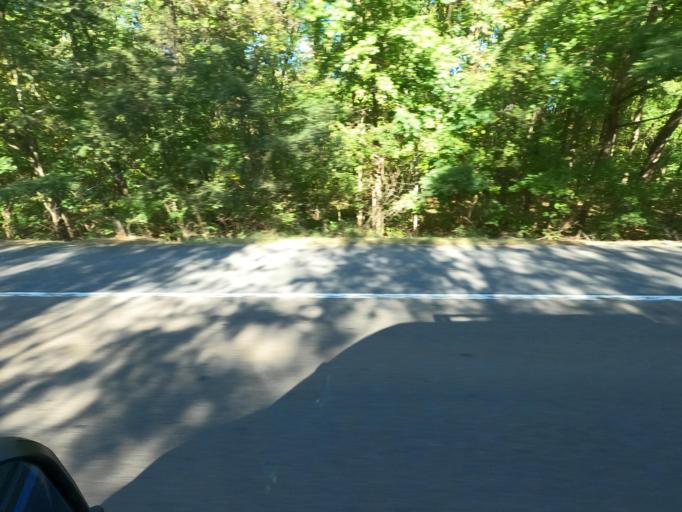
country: US
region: Tennessee
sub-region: Tipton County
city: Munford
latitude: 35.4350
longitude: -89.8023
